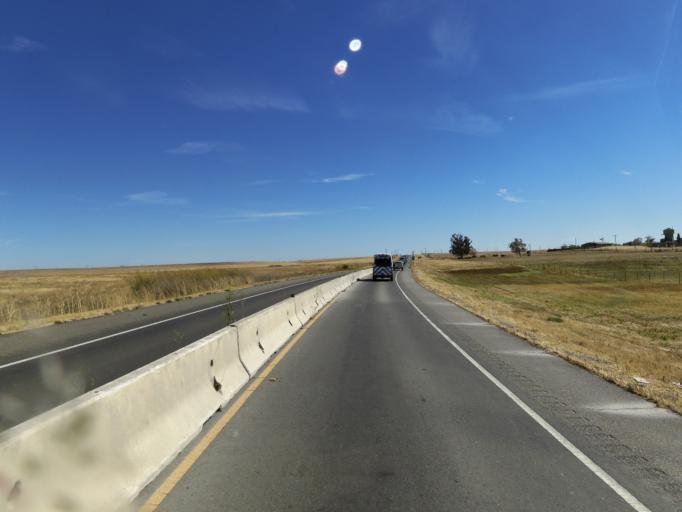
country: US
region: California
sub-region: Solano County
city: Suisun
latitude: 38.2267
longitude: -121.8947
